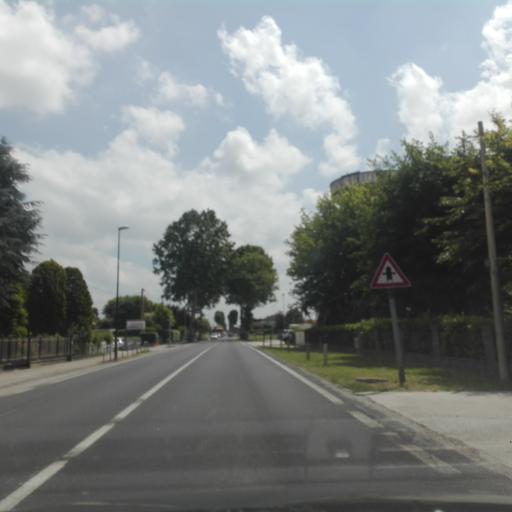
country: IT
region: Veneto
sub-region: Provincia di Rovigo
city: Villadose
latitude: 45.0657
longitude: 11.9006
